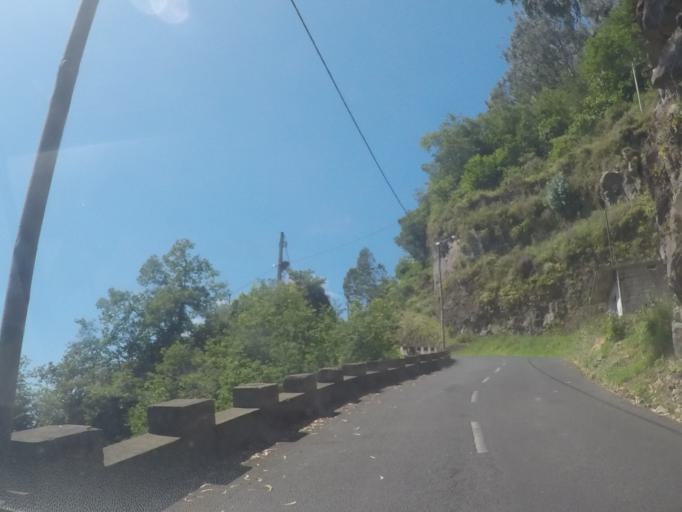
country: PT
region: Madeira
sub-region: Camara de Lobos
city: Curral das Freiras
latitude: 32.6921
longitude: -16.9709
